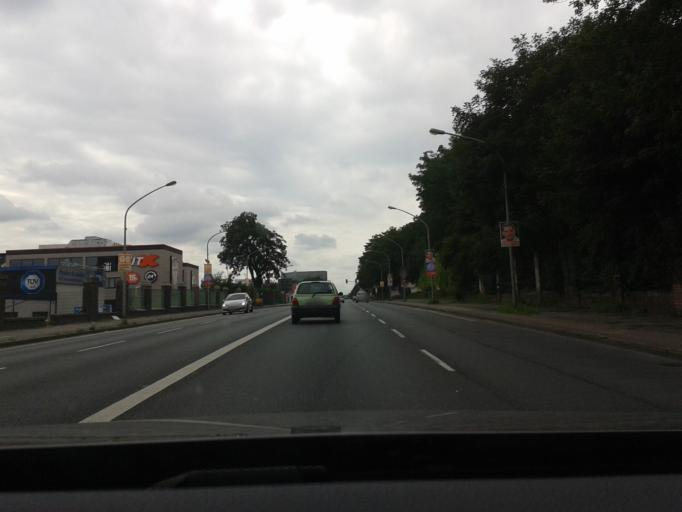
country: DE
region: North Rhine-Westphalia
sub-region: Regierungsbezirk Dusseldorf
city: Oberhausen
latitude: 51.4859
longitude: 6.8643
